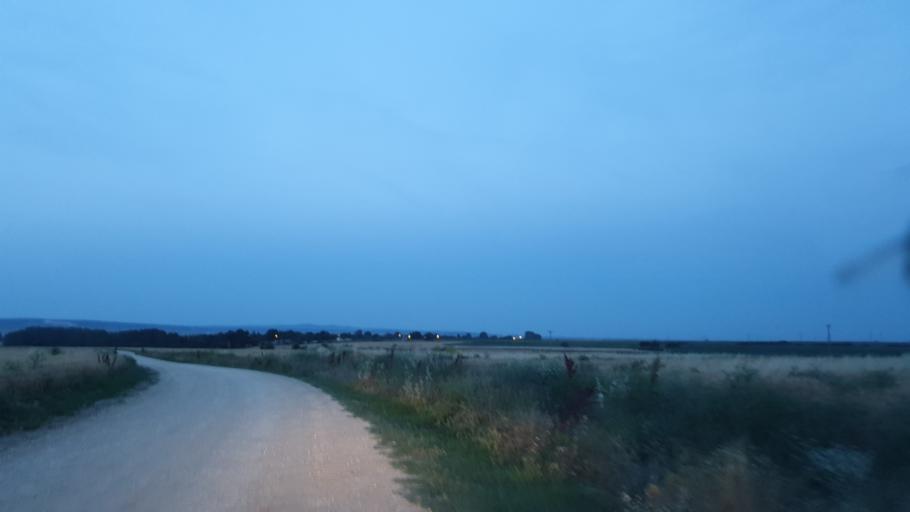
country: TR
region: Kirklareli
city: Vize
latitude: 41.5176
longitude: 27.7635
